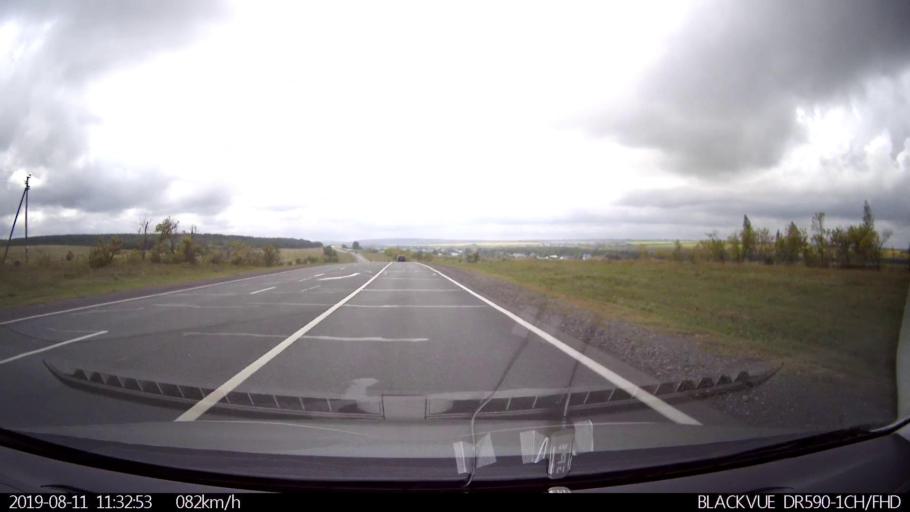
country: RU
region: Ulyanovsk
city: Krasnyy Gulyay
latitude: 54.0333
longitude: 48.2126
